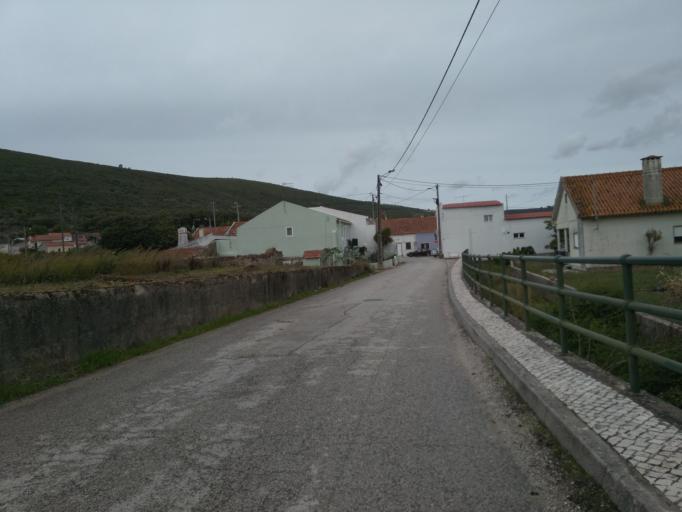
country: PT
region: Leiria
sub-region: Porto de Mos
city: Porto de Mos
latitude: 39.5852
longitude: -8.8203
